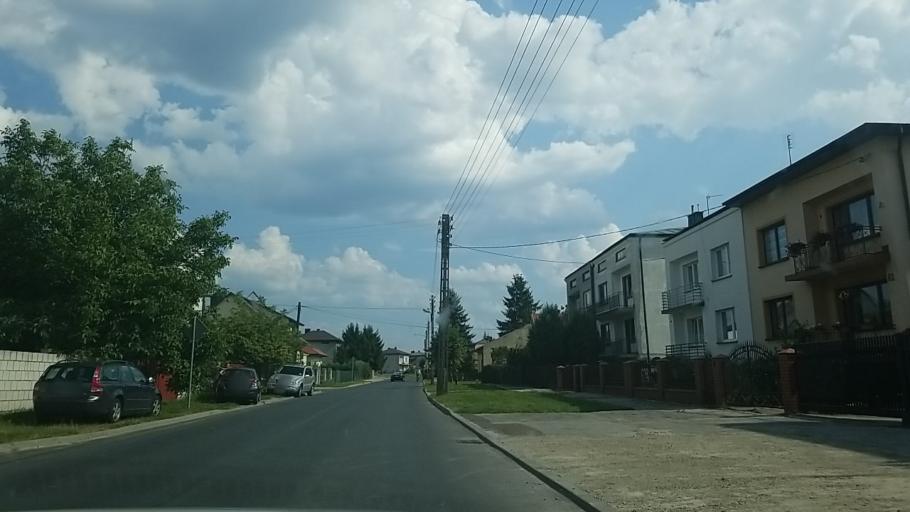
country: PL
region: Lublin Voivodeship
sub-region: Powiat janowski
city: Janow Lubelski
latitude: 50.7041
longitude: 22.4081
